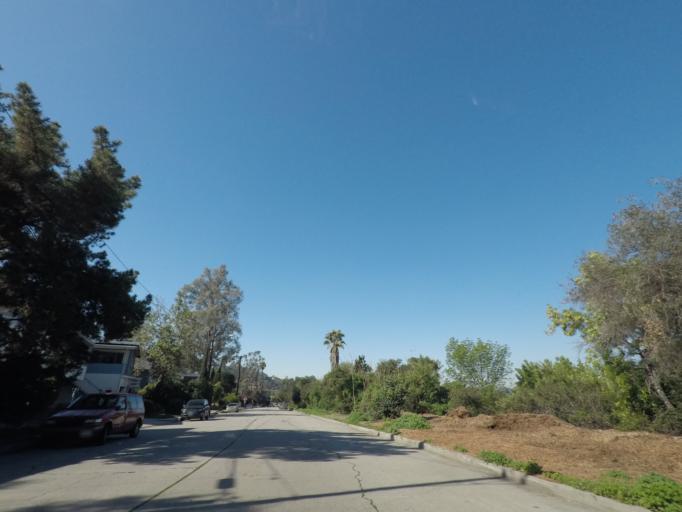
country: US
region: California
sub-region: Los Angeles County
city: South Pasadena
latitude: 34.1154
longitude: -118.1677
